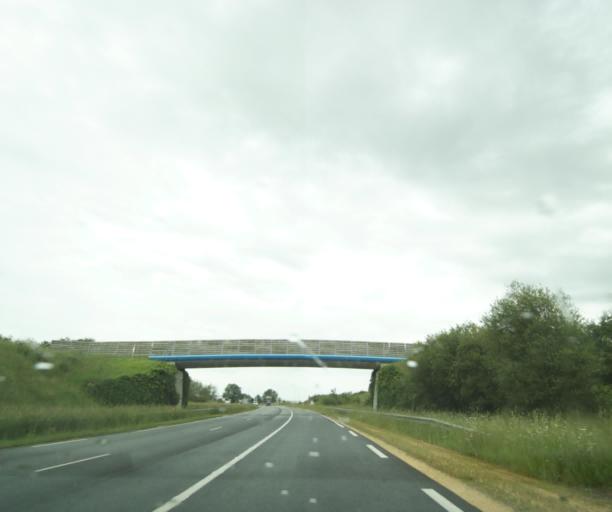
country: FR
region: Poitou-Charentes
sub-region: Departement des Deux-Sevres
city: Parthenay
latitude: 46.6621
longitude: -0.2525
